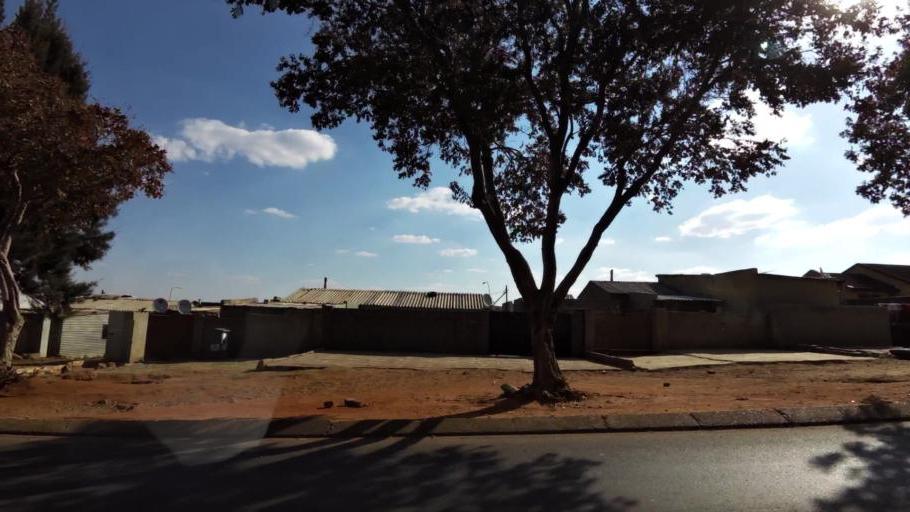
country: ZA
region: Gauteng
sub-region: City of Johannesburg Metropolitan Municipality
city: Soweto
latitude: -26.2195
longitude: 27.8894
